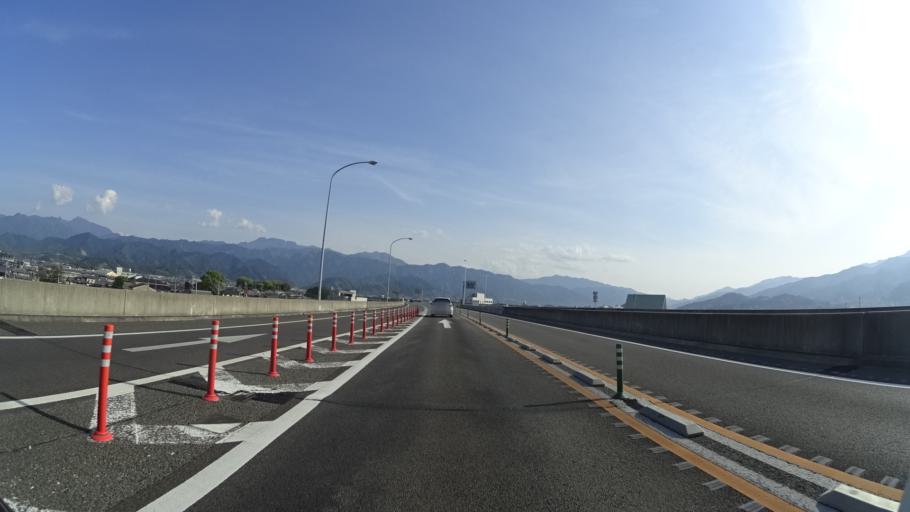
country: JP
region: Ehime
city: Saijo
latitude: 33.9166
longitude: 133.0731
